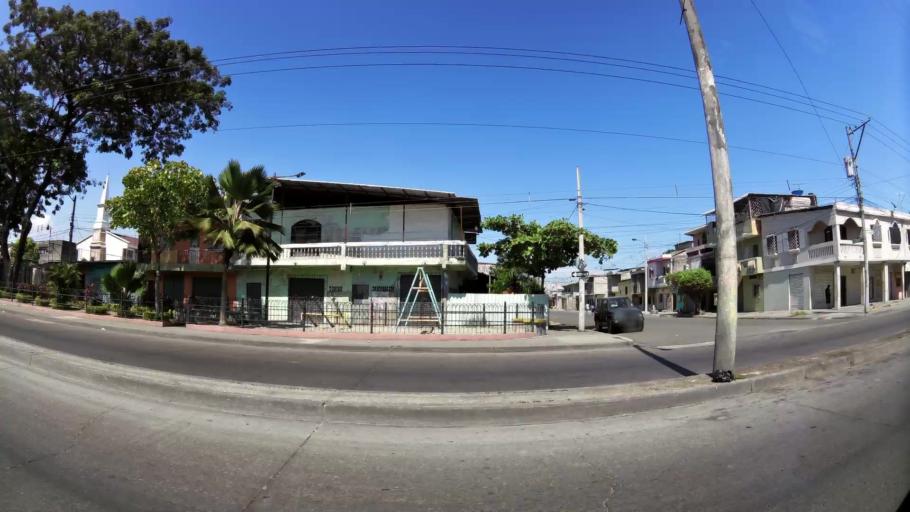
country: EC
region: Guayas
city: Guayaquil
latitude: -2.2212
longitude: -79.9401
